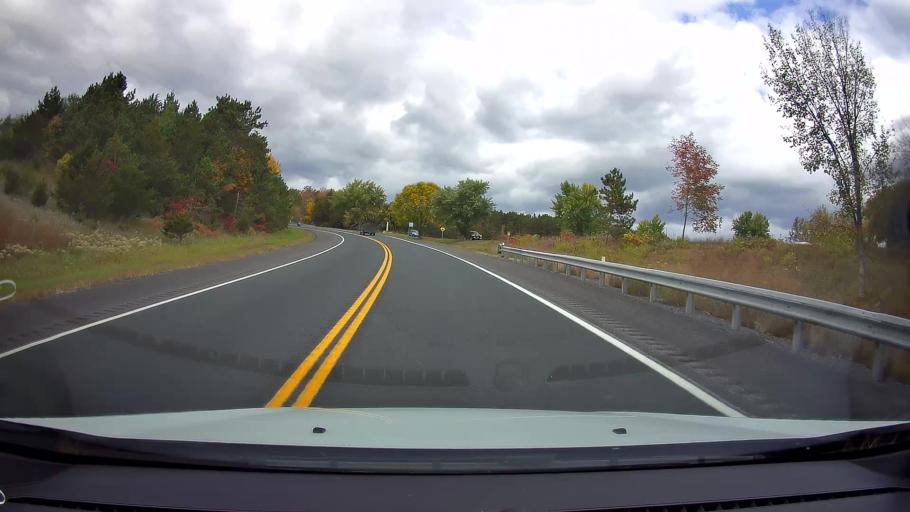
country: US
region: Wisconsin
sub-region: Polk County
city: Saint Croix Falls
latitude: 45.4169
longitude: -92.6539
